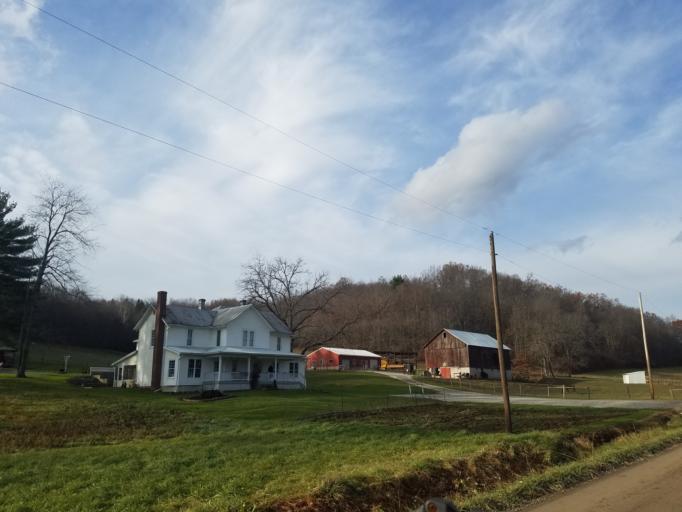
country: US
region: Ohio
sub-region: Knox County
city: Danville
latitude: 40.4635
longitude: -82.2075
